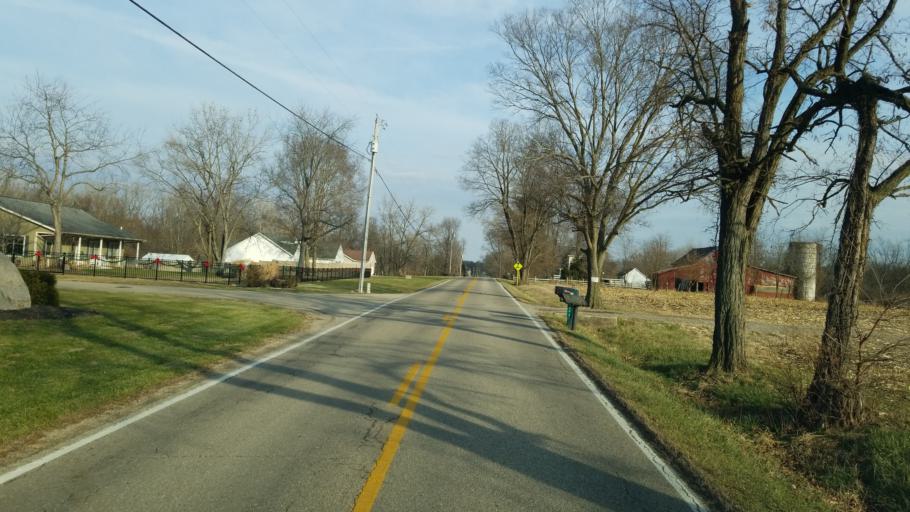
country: US
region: Ohio
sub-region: Ross County
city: Kingston
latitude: 39.4182
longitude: -82.9402
